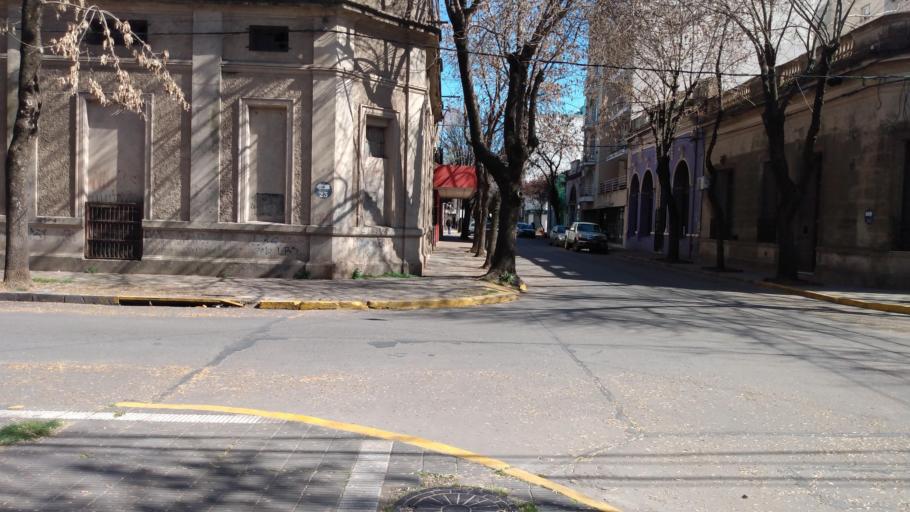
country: AR
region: Buenos Aires
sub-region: Partido de Mercedes
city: Mercedes
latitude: -34.6509
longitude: -59.4291
